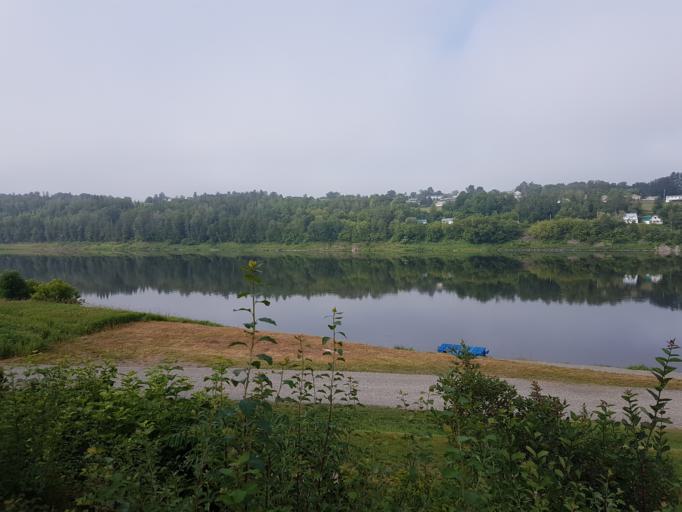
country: CA
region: New Brunswick
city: Florenceville-Bristol
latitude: 46.2969
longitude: -67.5277
